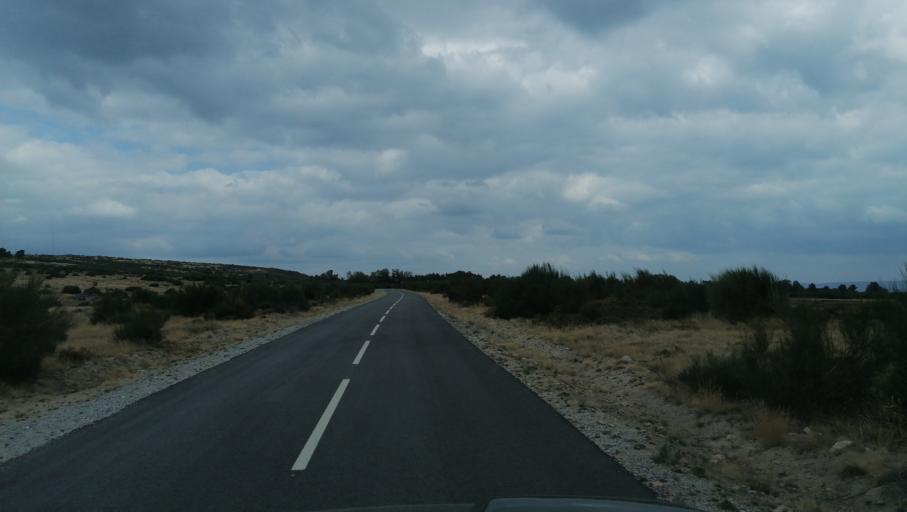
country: PT
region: Vila Real
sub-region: Vila Pouca de Aguiar
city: Vila Pouca de Aguiar
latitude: 41.5411
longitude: -7.6771
